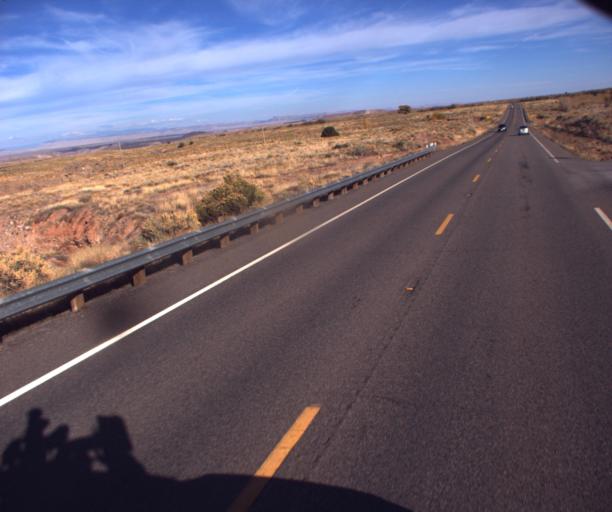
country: US
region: Arizona
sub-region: Apache County
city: Lukachukai
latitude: 36.9270
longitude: -109.1857
